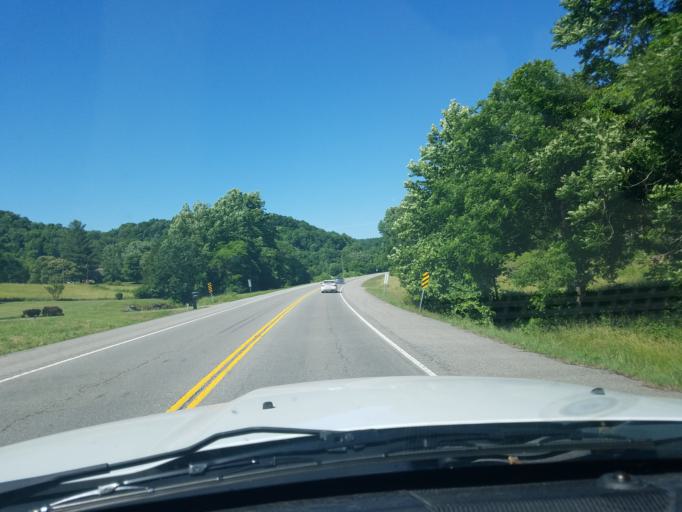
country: US
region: Tennessee
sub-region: Sumner County
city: Westmoreland
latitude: 36.5246
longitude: -86.2535
